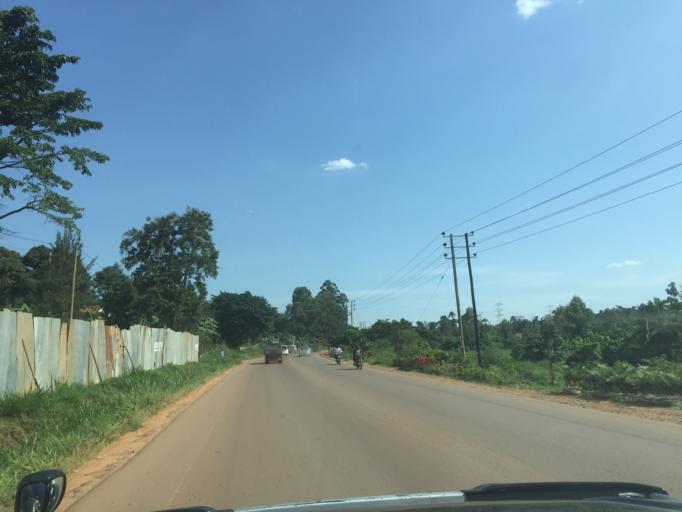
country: UG
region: Central Region
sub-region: Wakiso District
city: Wakiso
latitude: 0.4248
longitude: 32.5356
